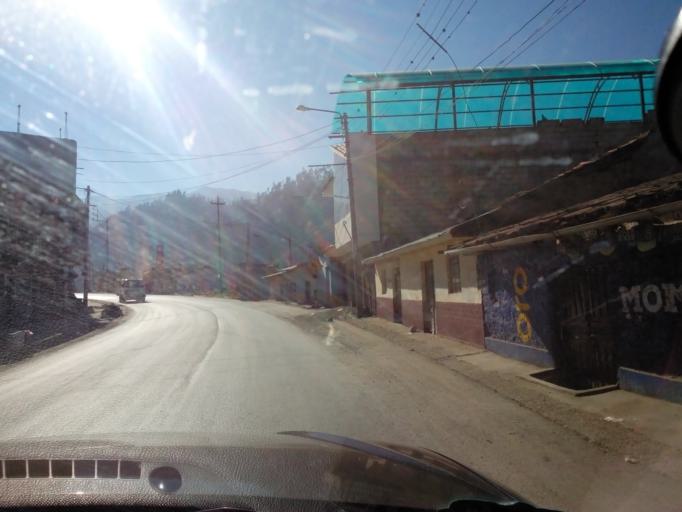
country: PE
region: Apurimac
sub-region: Provincia de Abancay
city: Tamburco
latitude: -13.6240
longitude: -72.8725
